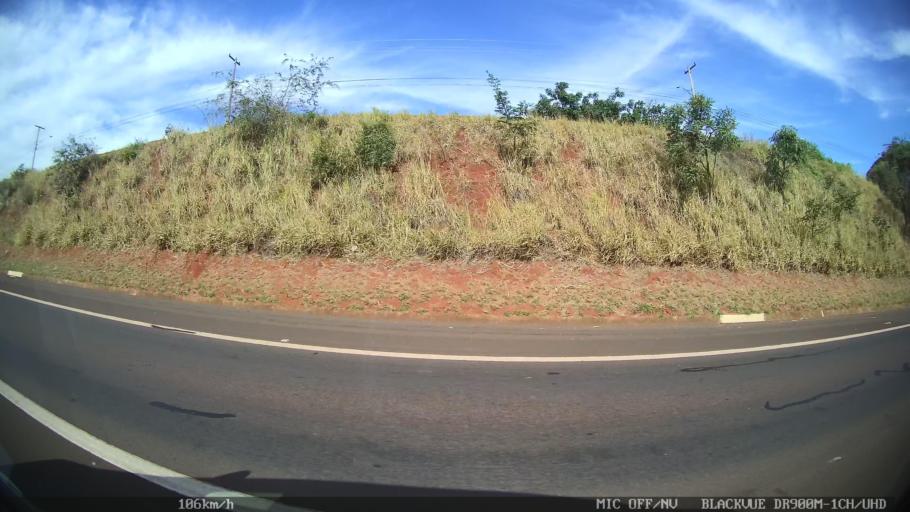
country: BR
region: Sao Paulo
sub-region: Araraquara
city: Araraquara
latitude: -21.8017
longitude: -48.1456
